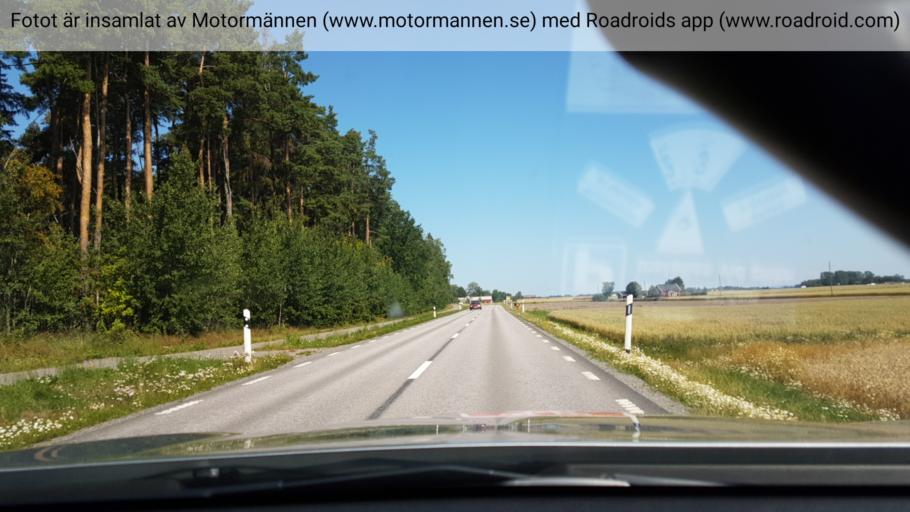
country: SE
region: Vaestra Goetaland
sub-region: Vara Kommun
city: Vara
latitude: 58.2838
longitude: 12.9583
